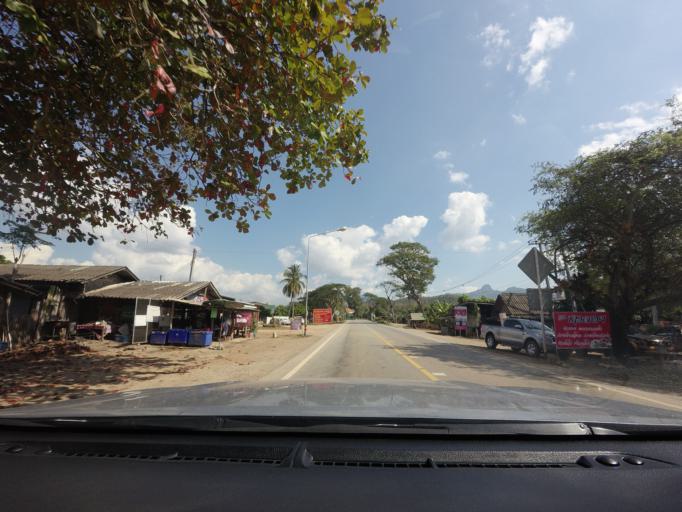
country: TH
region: Chiang Mai
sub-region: Amphoe Chiang Dao
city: Chiang Dao
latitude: 19.4818
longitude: 99.0197
